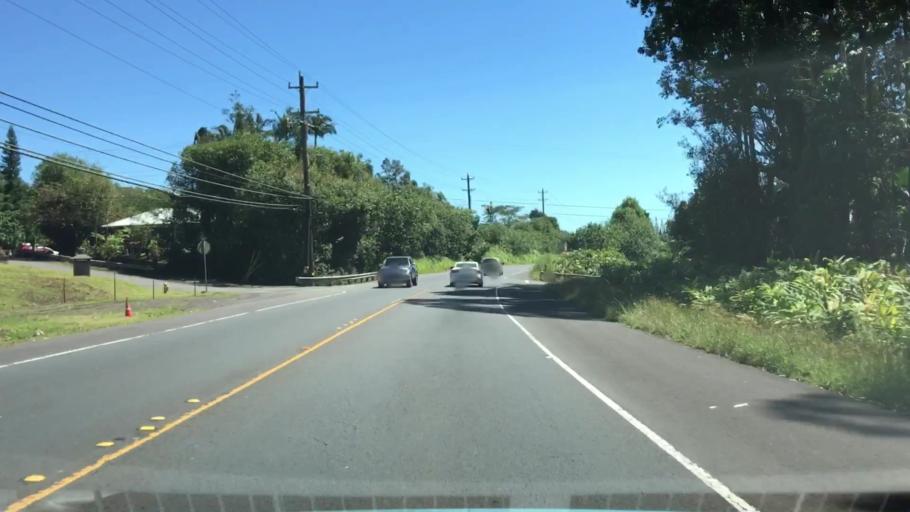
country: US
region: Hawaii
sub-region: Hawaii County
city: Mountain View
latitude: 19.5470
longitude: -155.1124
